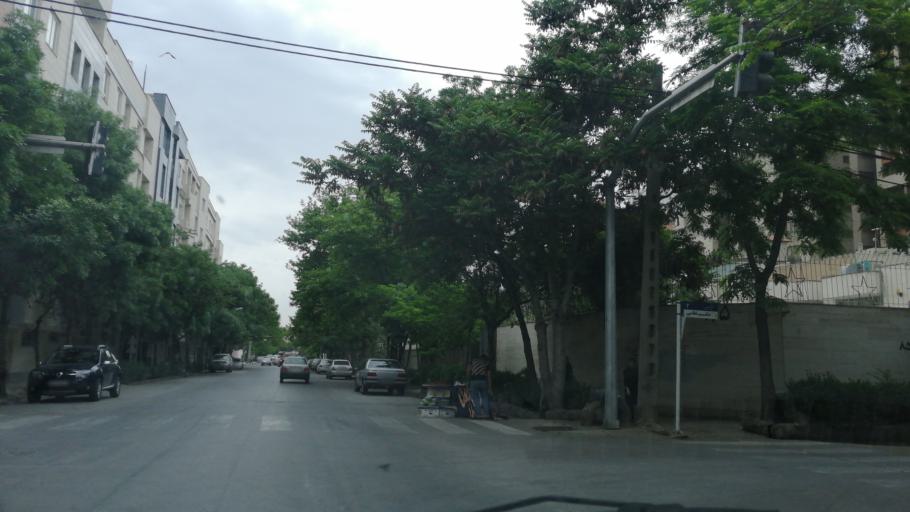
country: IR
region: Razavi Khorasan
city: Mashhad
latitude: 36.2847
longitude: 59.5713
